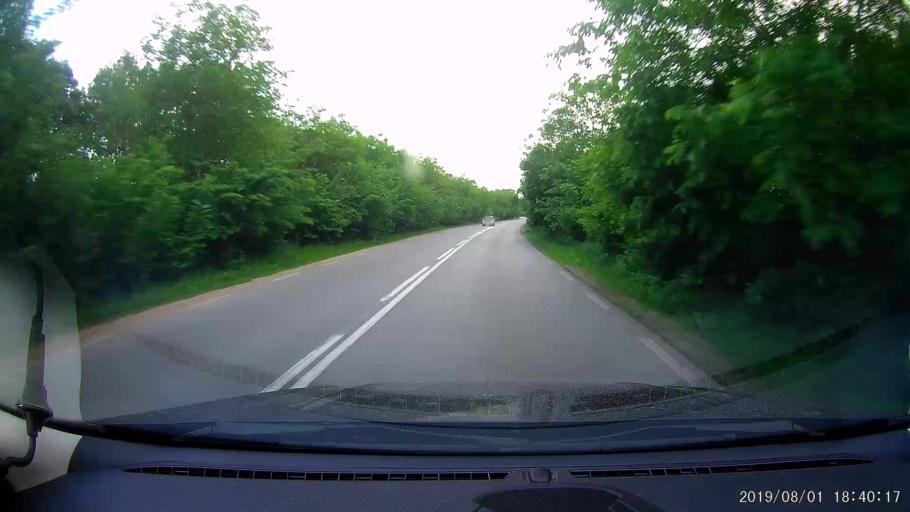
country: BG
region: Shumen
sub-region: Obshtina Khitrino
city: Gara Khitrino
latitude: 43.3703
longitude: 26.9199
